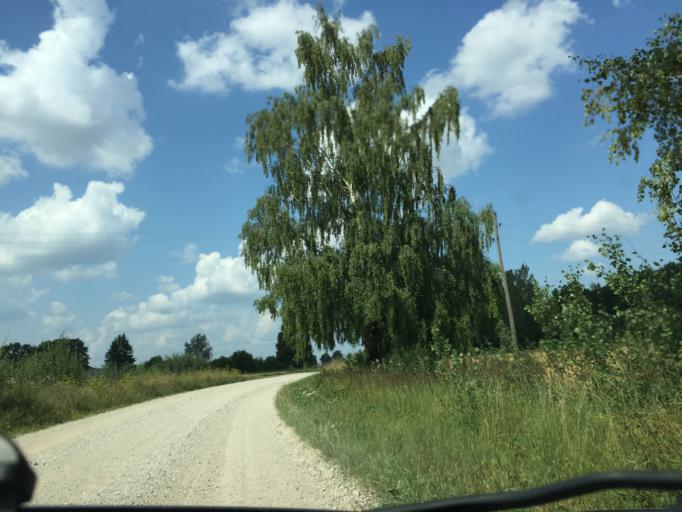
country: LT
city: Zagare
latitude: 56.3899
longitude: 23.2556
